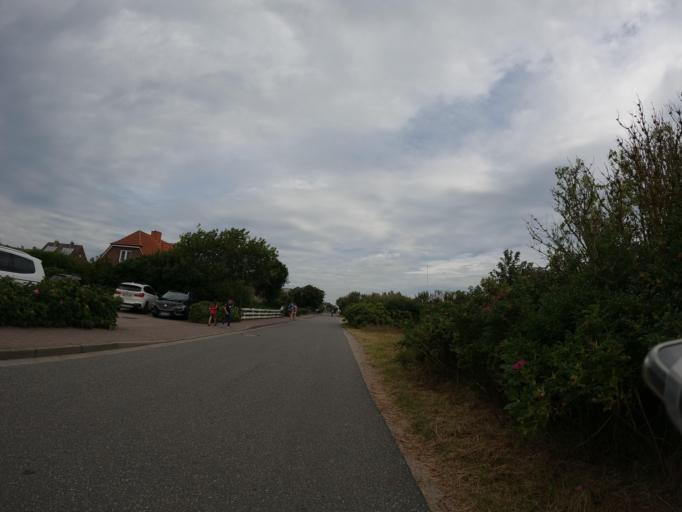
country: DE
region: Schleswig-Holstein
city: Westerland
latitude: 54.9318
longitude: 8.3265
